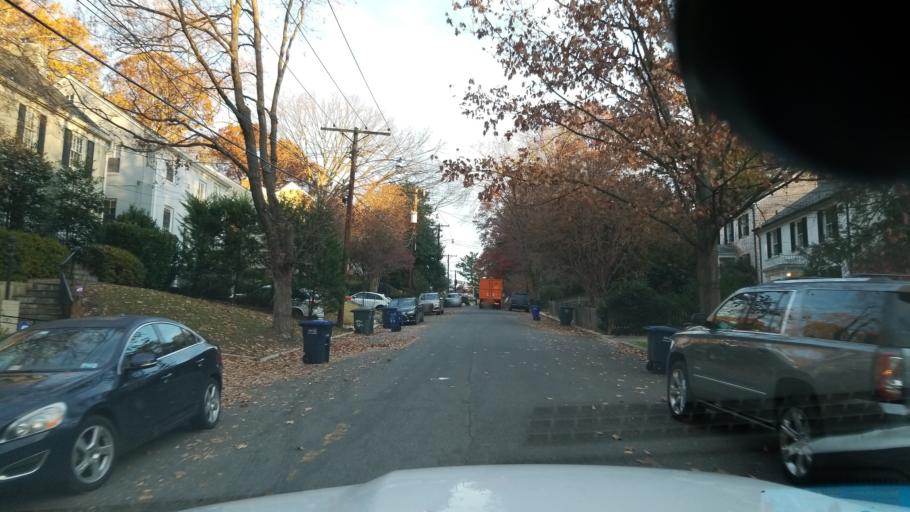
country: US
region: Maryland
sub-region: Montgomery County
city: Brookmont
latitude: 38.9205
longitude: -77.0944
